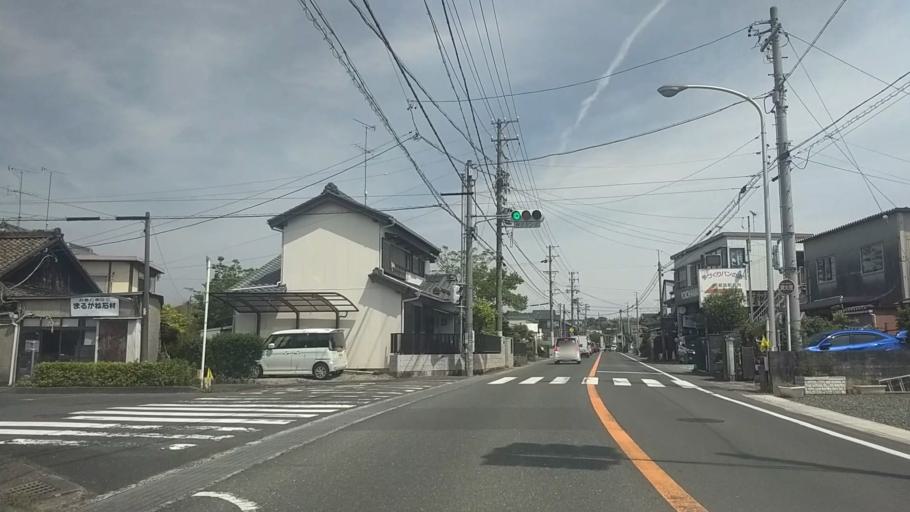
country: JP
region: Shizuoka
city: Kosai-shi
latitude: 34.7954
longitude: 137.5739
